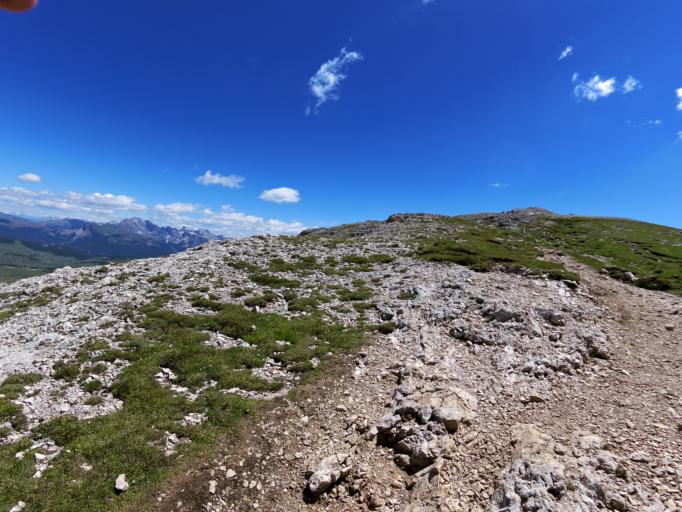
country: IT
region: Trentino-Alto Adige
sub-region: Bolzano
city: Siusi
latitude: 46.5008
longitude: 11.6065
